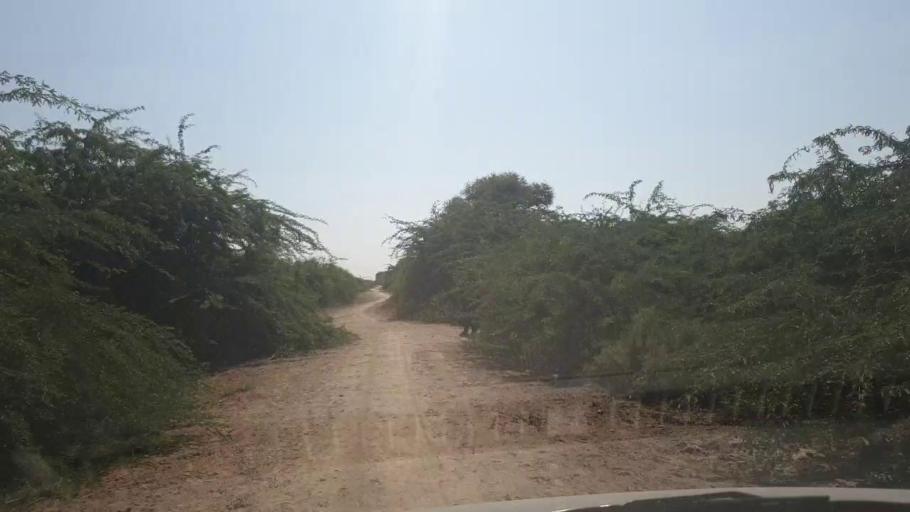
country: PK
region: Sindh
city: Tando Bago
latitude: 24.9040
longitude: 69.1644
